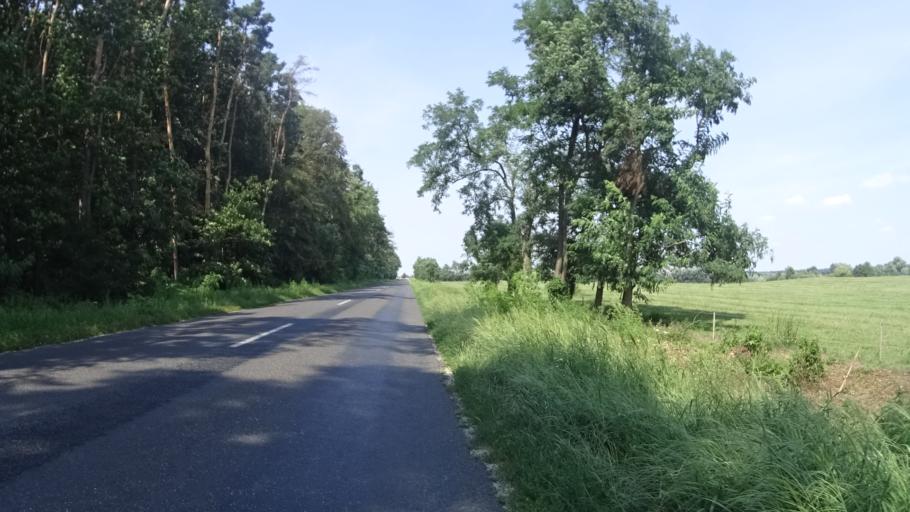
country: HU
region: Zala
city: Nagykanizsa
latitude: 46.4166
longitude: 16.9499
